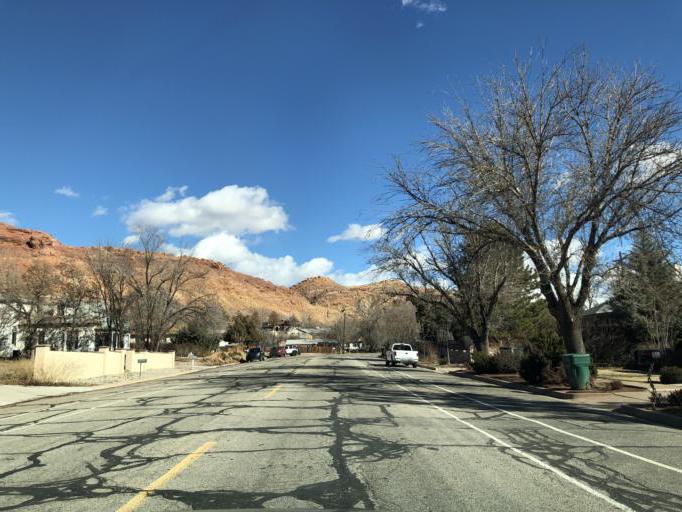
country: US
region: Utah
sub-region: Grand County
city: Moab
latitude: 38.5764
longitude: -109.5481
